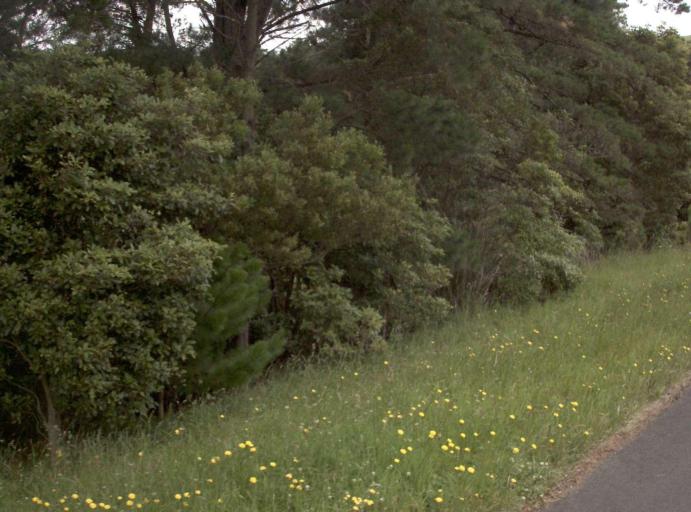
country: AU
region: Victoria
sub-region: Latrobe
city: Moe
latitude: -38.6164
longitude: 146.1380
